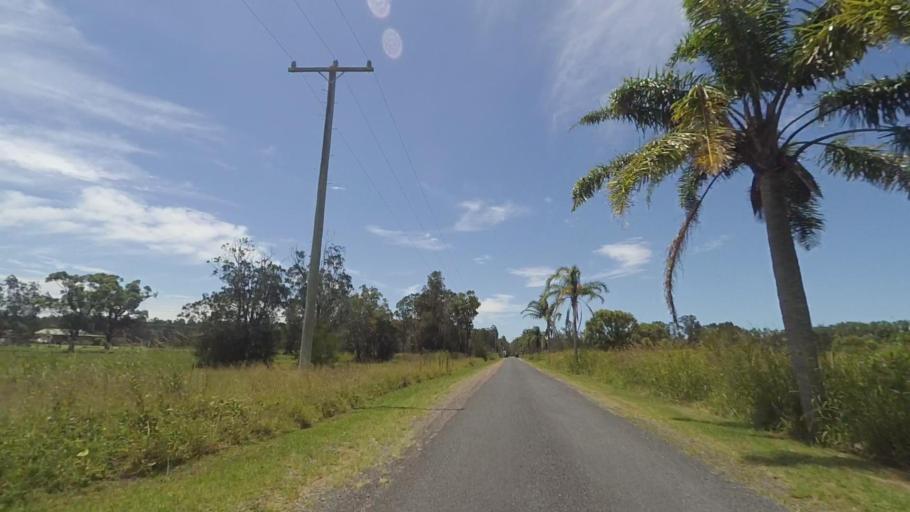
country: AU
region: New South Wales
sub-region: Port Stephens Shire
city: Anna Bay
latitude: -32.7698
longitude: 152.0022
